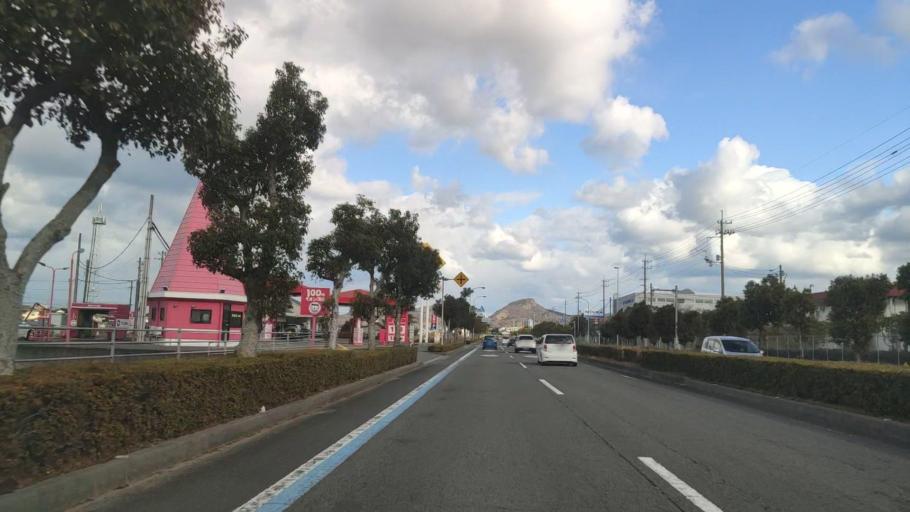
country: JP
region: Ehime
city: Hojo
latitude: 33.9608
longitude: 132.7775
